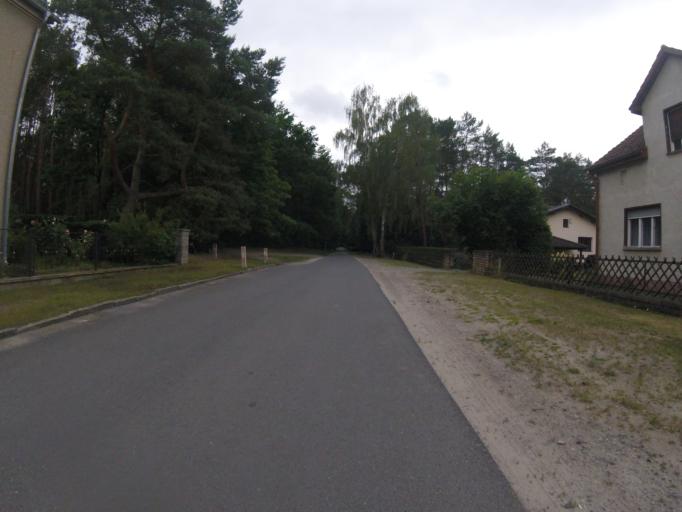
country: DE
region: Brandenburg
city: Bestensee
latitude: 52.2327
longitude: 13.6279
